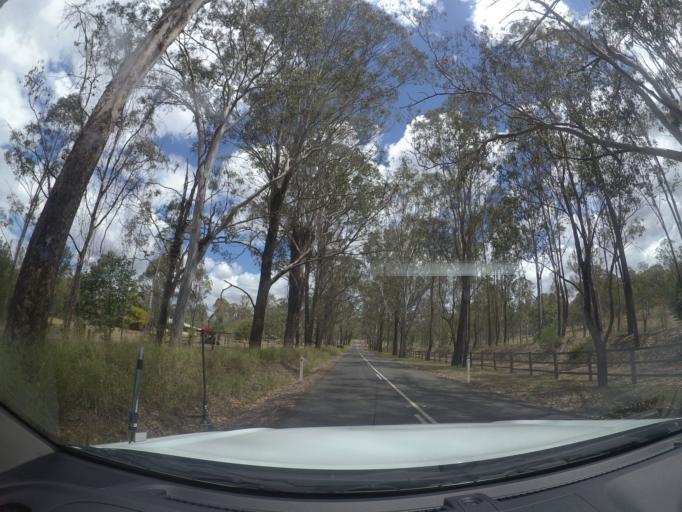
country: AU
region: Queensland
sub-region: Logan
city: Cedar Vale
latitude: -27.9371
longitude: 153.0698
